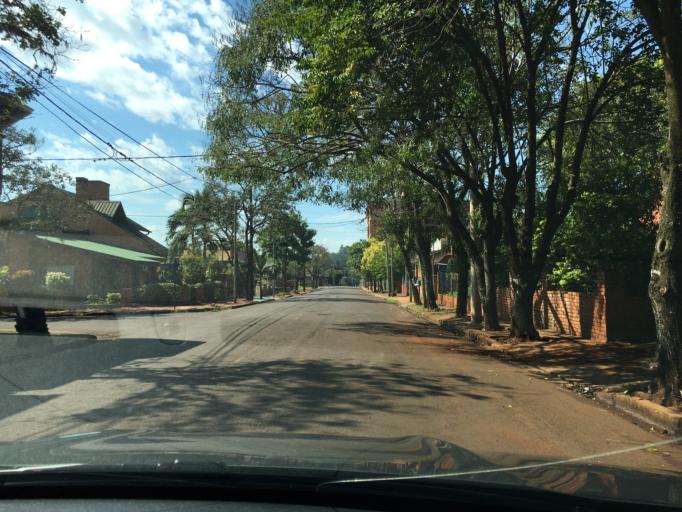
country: AR
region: Misiones
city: Puerto Rico
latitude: -26.8166
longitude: -55.0238
